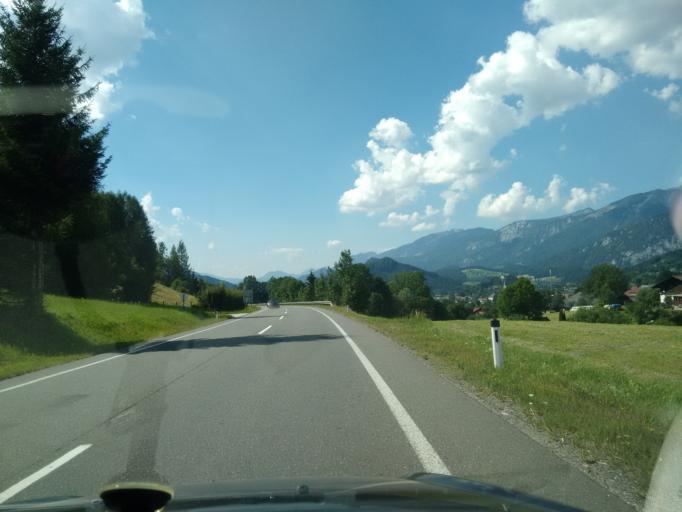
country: AT
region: Upper Austria
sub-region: Politischer Bezirk Kirchdorf an der Krems
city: Rossleithen
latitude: 47.7104
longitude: 14.3385
